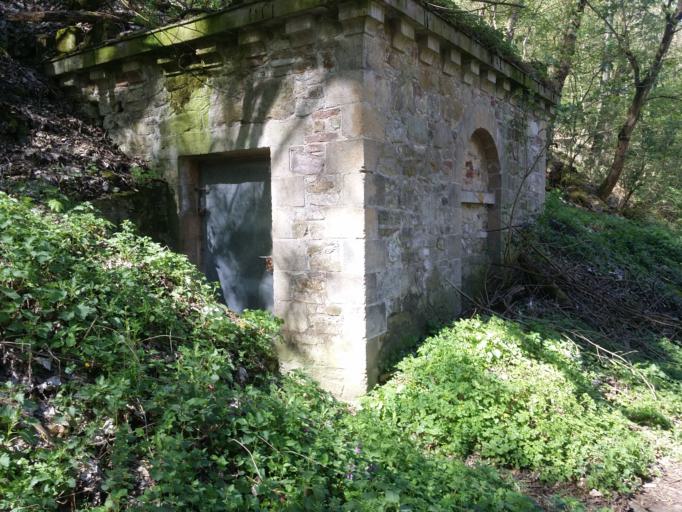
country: DE
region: Saxony-Anhalt
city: Ballenstedt
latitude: 51.6834
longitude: 11.2664
